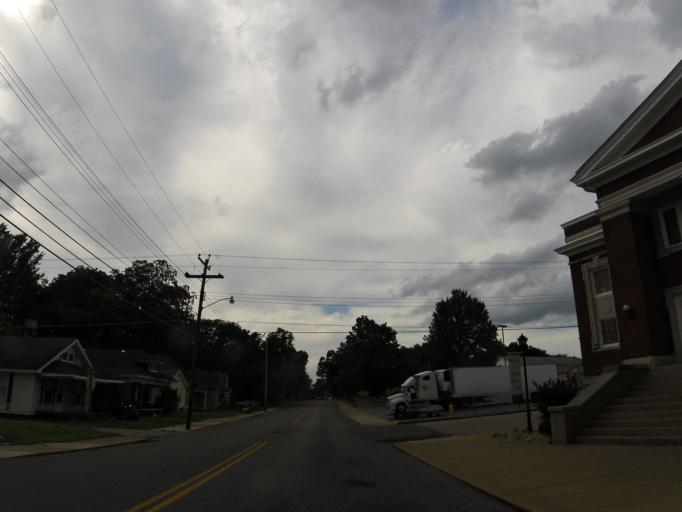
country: US
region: Kentucky
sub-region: Christian County
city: Hopkinsville
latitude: 36.8688
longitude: -87.4946
